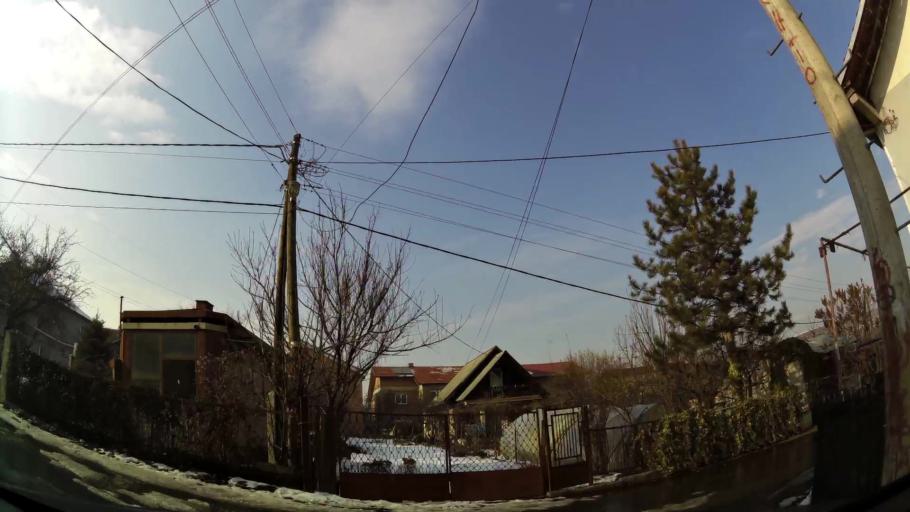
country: MK
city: Creshevo
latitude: 42.0107
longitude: 21.4980
